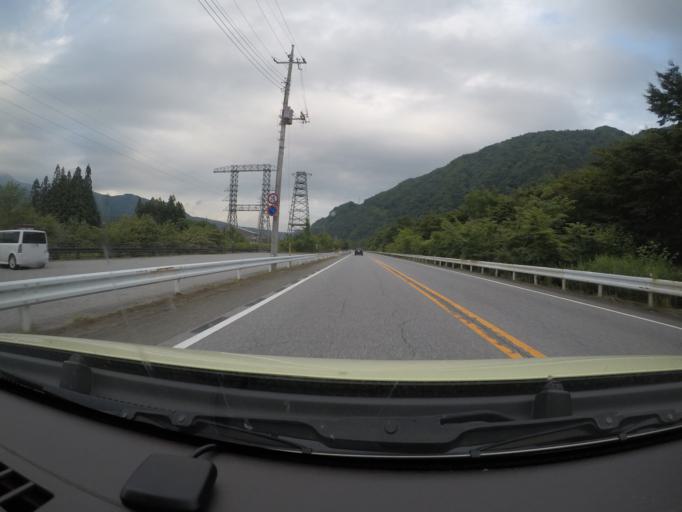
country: JP
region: Tochigi
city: Nikko
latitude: 36.7331
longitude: 139.5583
